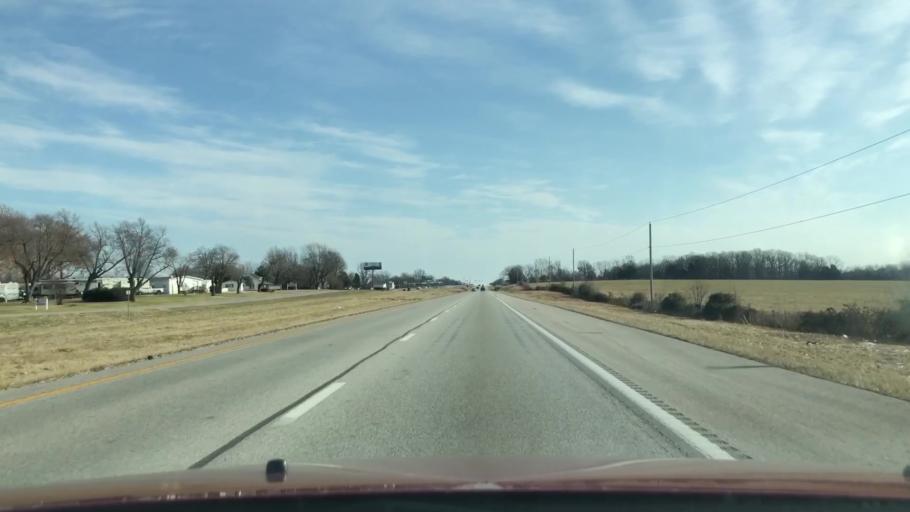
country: US
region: Missouri
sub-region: Webster County
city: Rogersville
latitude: 37.1189
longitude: -93.1308
